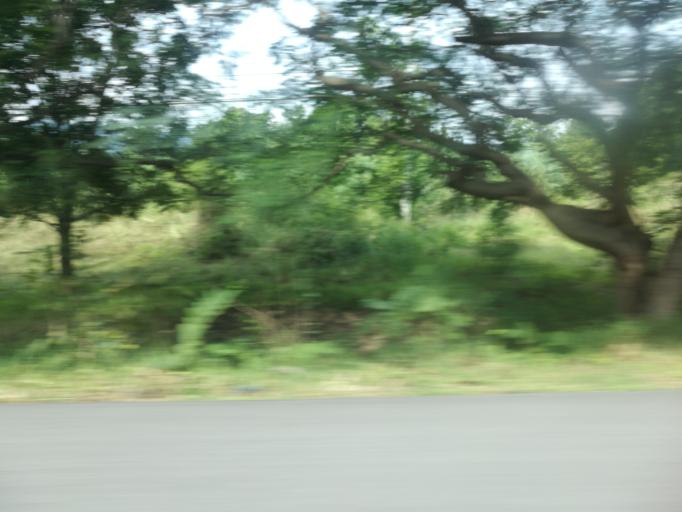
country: TH
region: Phetchaburi
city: Cha-am
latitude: 12.7493
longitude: 99.9310
